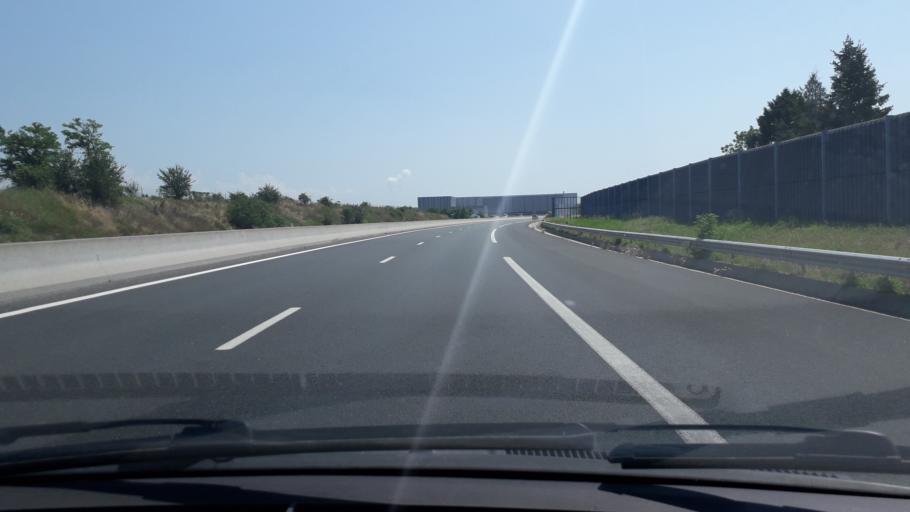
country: FR
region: Rhone-Alpes
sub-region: Departement du Rhone
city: Pusignan
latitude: 45.7667
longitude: 5.0680
